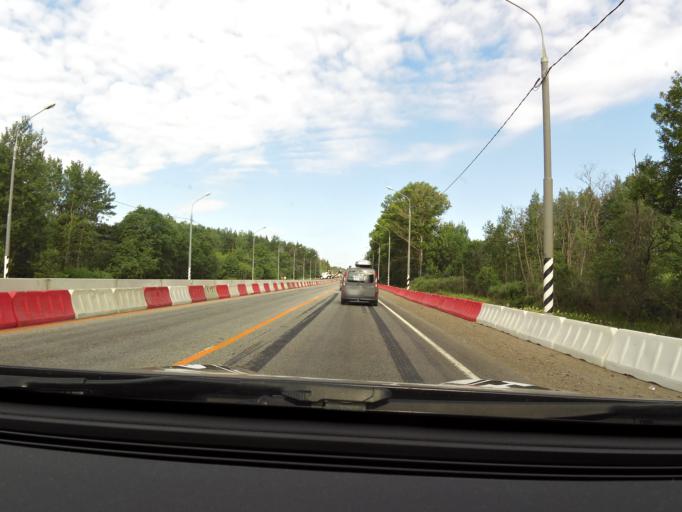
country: RU
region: Tverskaya
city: Emmaus
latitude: 56.7601
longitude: 36.1758
